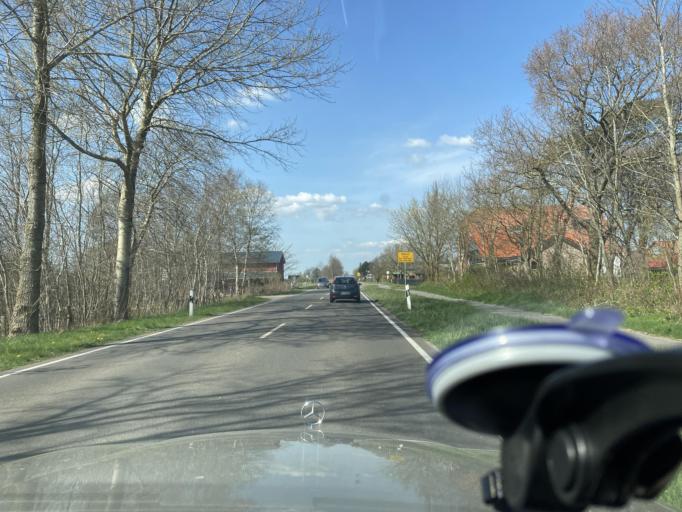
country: DE
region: Schleswig-Holstein
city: Krempel
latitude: 54.2935
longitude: 9.0410
